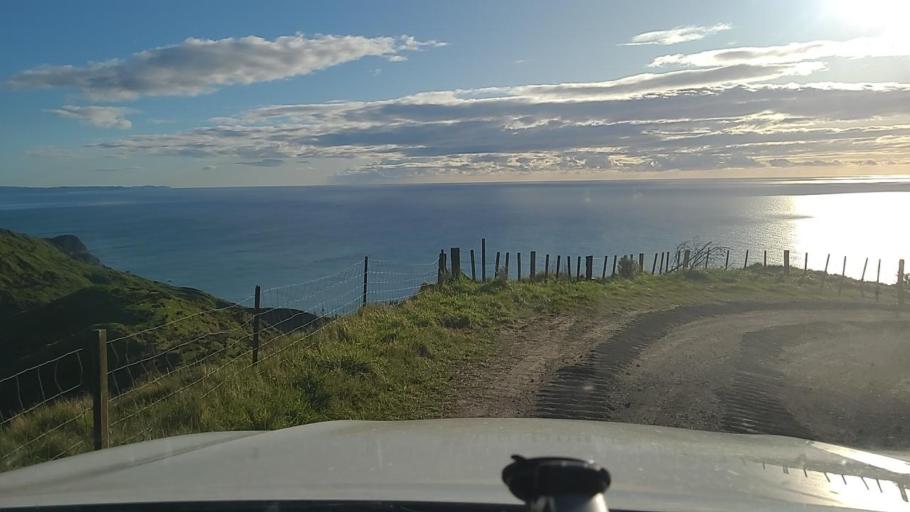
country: NZ
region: Gisborne
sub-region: Gisborne District
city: Gisborne
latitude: -38.9467
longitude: 177.8913
